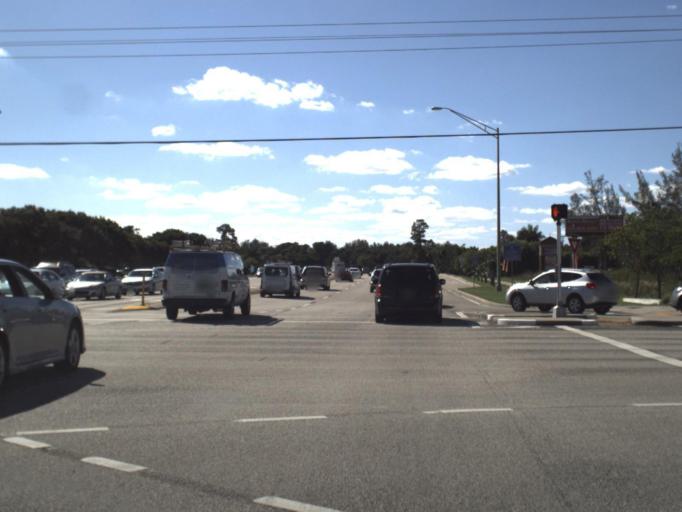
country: US
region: Florida
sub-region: Lee County
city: Villas
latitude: 26.5281
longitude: -81.8712
